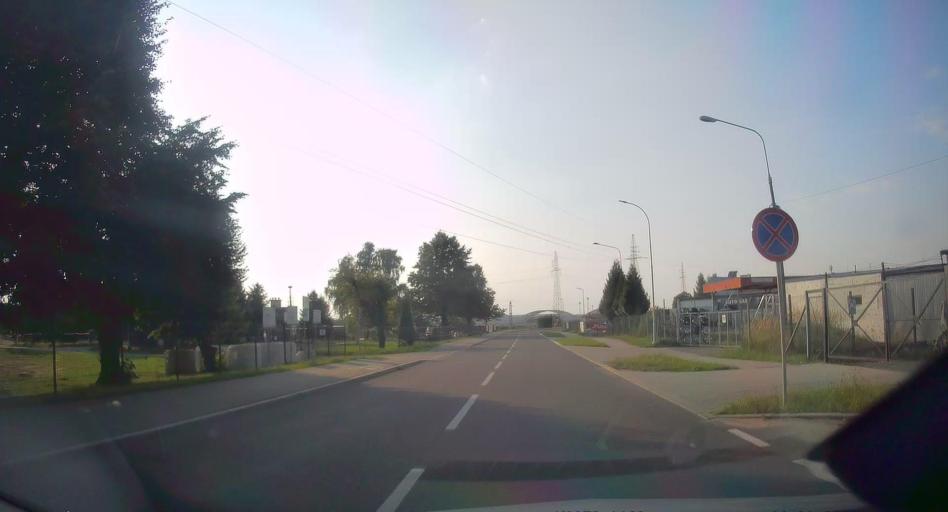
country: PL
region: Subcarpathian Voivodeship
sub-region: Powiat debicki
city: Debica
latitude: 50.0425
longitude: 21.3823
